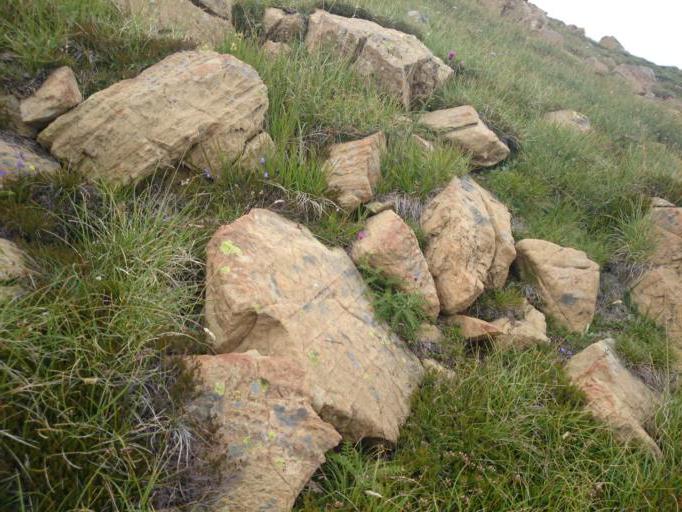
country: AL
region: Diber
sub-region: Rrethi i Dibres
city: Fushe-Lure
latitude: 41.7852
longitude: 20.1820
